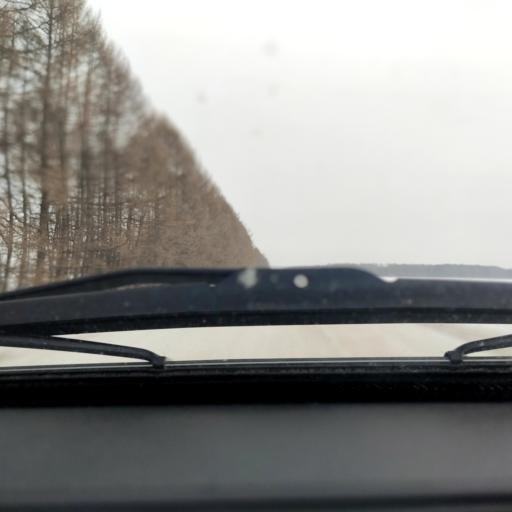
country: RU
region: Bashkortostan
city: Mikhaylovka
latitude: 54.8544
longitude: 55.8598
